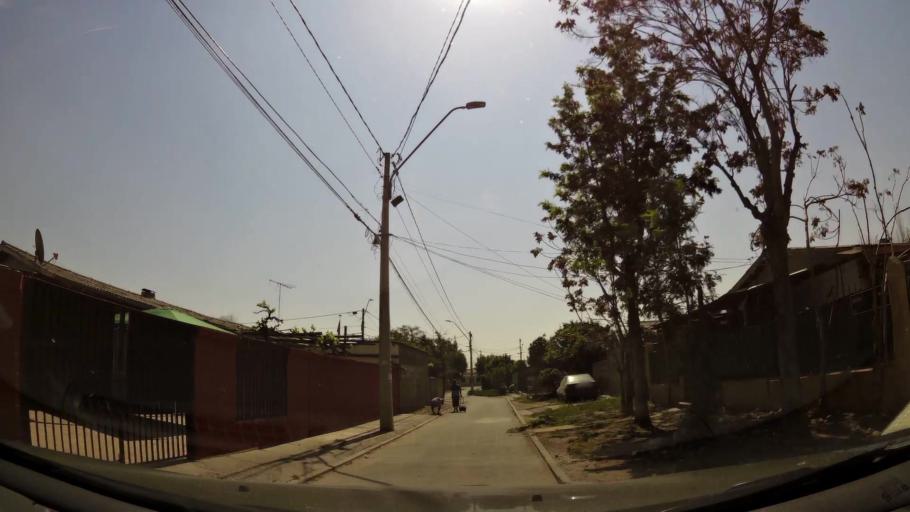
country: CL
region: Santiago Metropolitan
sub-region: Provincia de Maipo
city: San Bernardo
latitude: -33.5860
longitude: -70.7104
